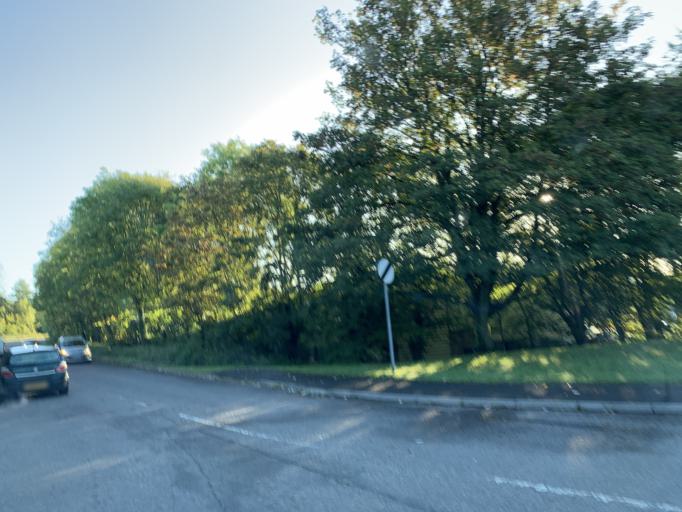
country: GB
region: England
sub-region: Wiltshire
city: Alderbury
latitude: 51.0352
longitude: -1.7206
